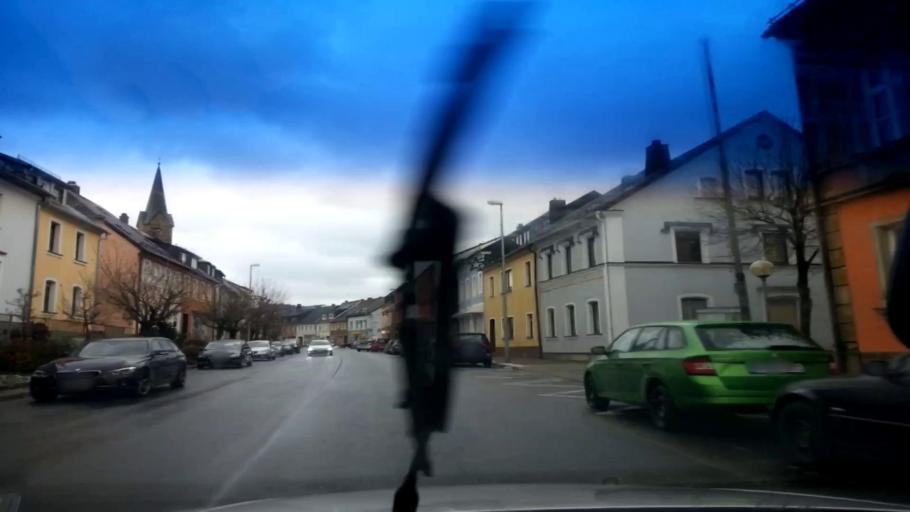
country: DE
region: Bavaria
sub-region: Upper Franconia
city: Gefrees
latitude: 50.0951
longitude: 11.7362
